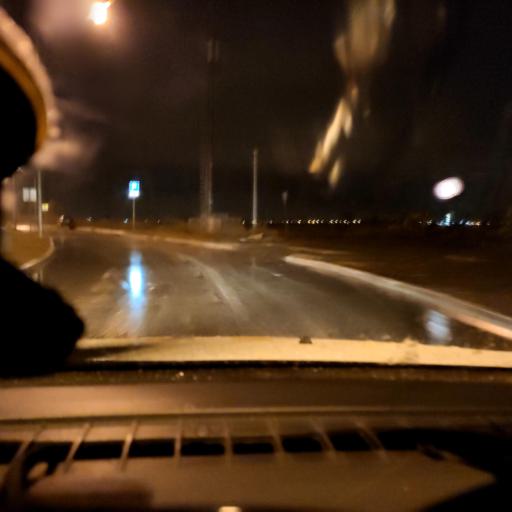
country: RU
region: Samara
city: Samara
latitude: 53.1162
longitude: 50.1530
